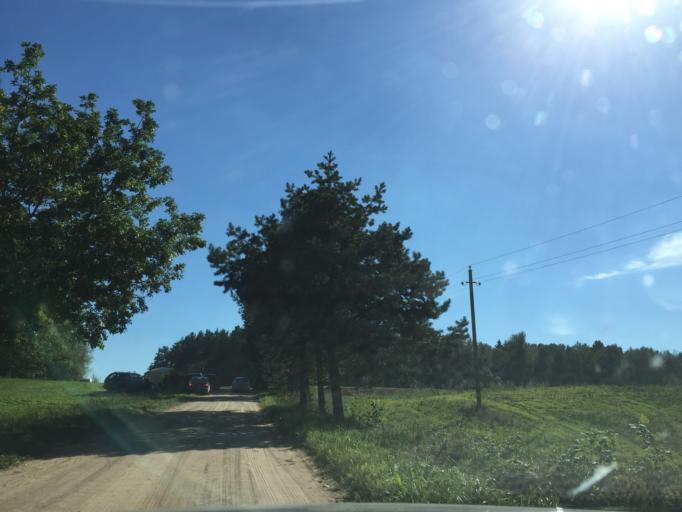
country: LT
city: Zarasai
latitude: 55.7887
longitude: 25.9538
